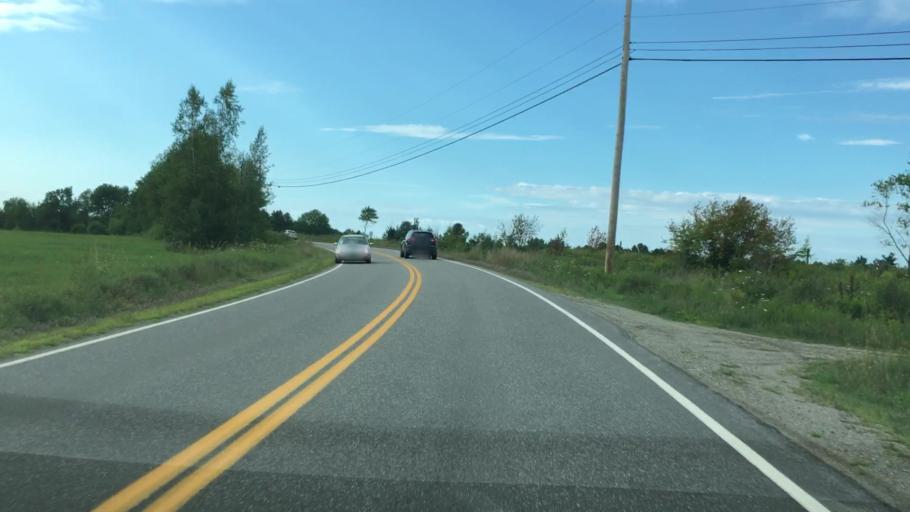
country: US
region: Maine
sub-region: Waldo County
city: Belfast
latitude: 44.3755
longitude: -69.0315
